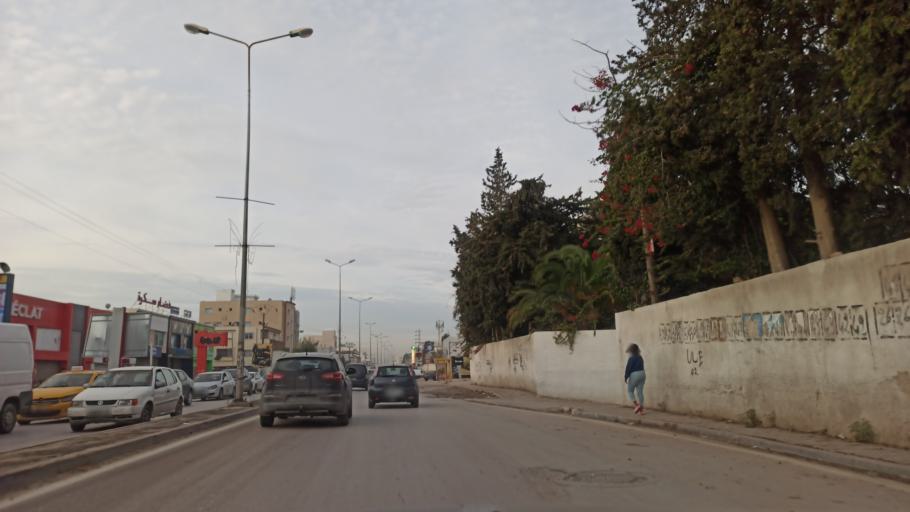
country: TN
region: Ariana
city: Ariana
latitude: 36.8673
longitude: 10.2235
